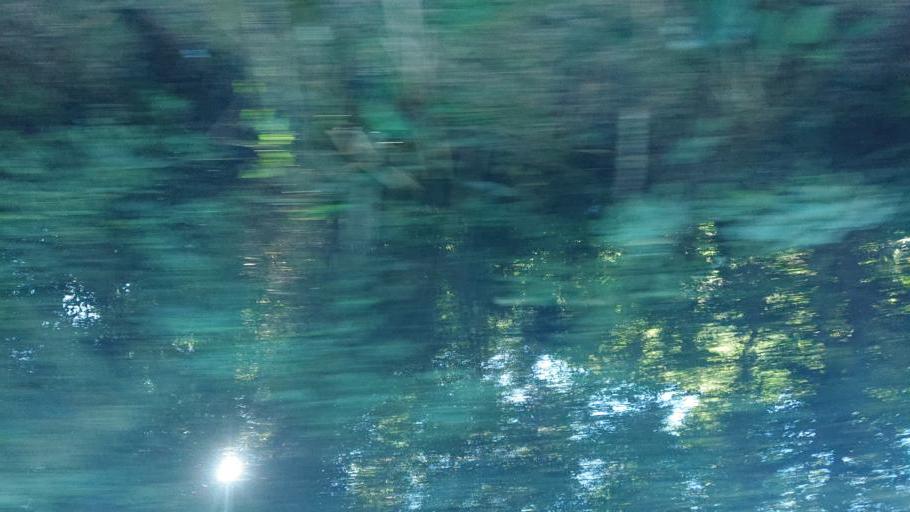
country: TW
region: Taiwan
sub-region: Chiayi
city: Jiayi Shi
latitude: 23.5273
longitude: 120.6271
